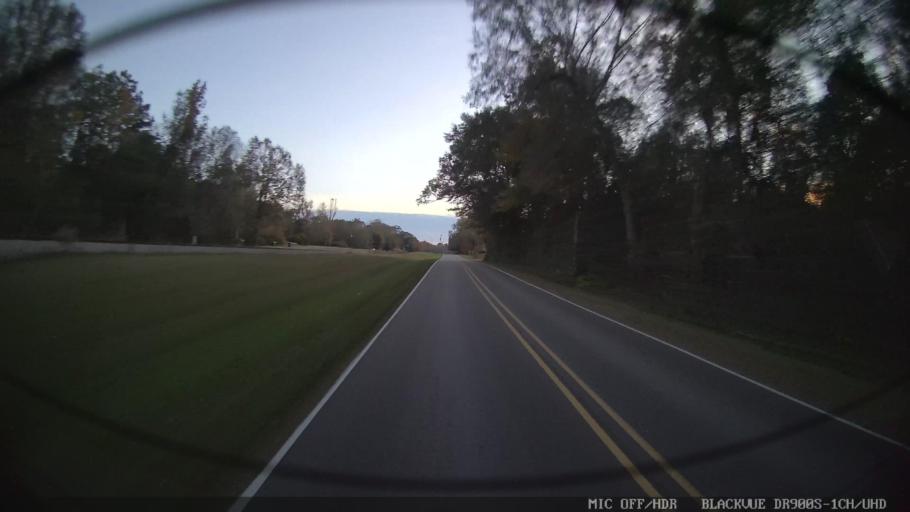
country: US
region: Mississippi
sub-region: Perry County
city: New Augusta
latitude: 31.0642
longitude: -89.1867
